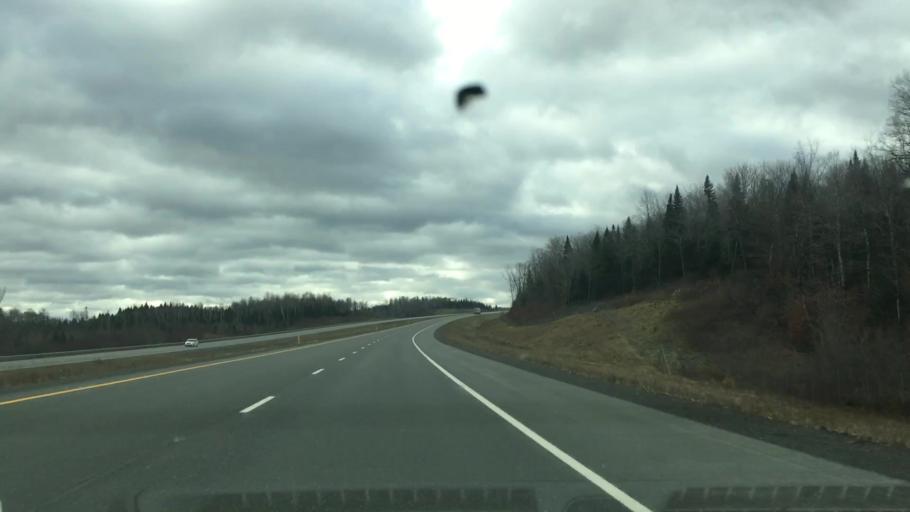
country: US
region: Maine
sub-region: Aroostook County
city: Fort Fairfield
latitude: 46.6678
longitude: -67.7298
